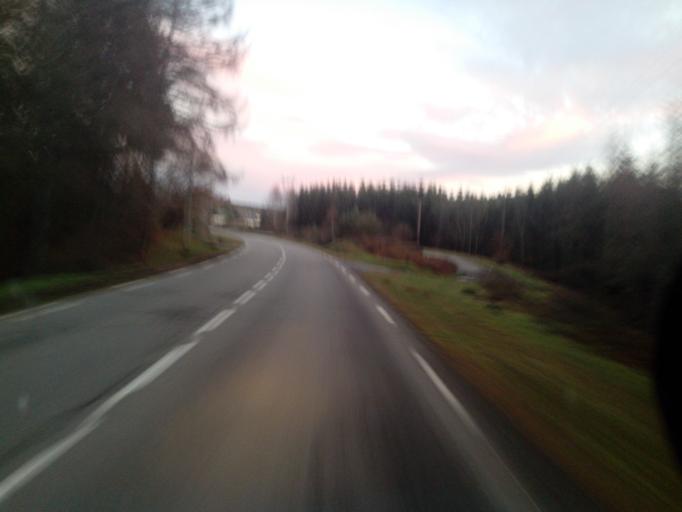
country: FR
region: Limousin
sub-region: Departement de la Correze
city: Meymac
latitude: 45.5034
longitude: 2.2175
